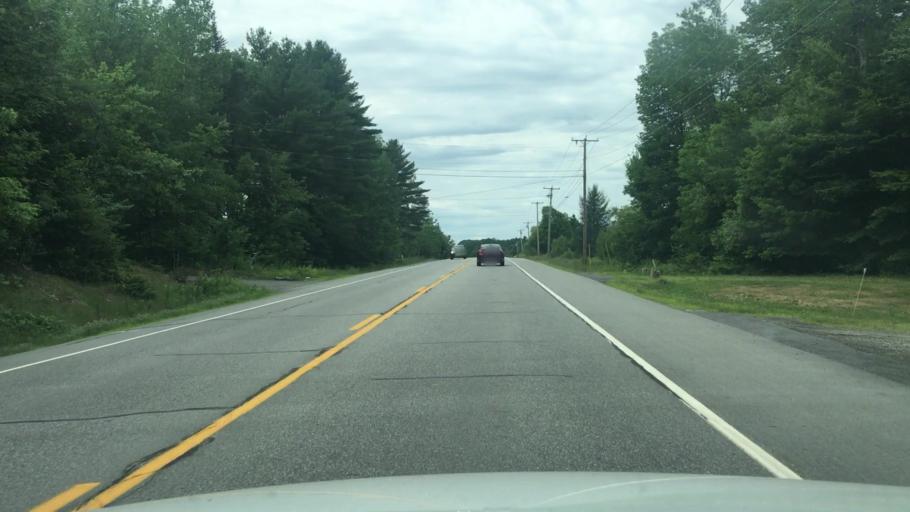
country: US
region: Maine
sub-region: Waldo County
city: Palermo
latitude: 44.4015
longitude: -69.5550
